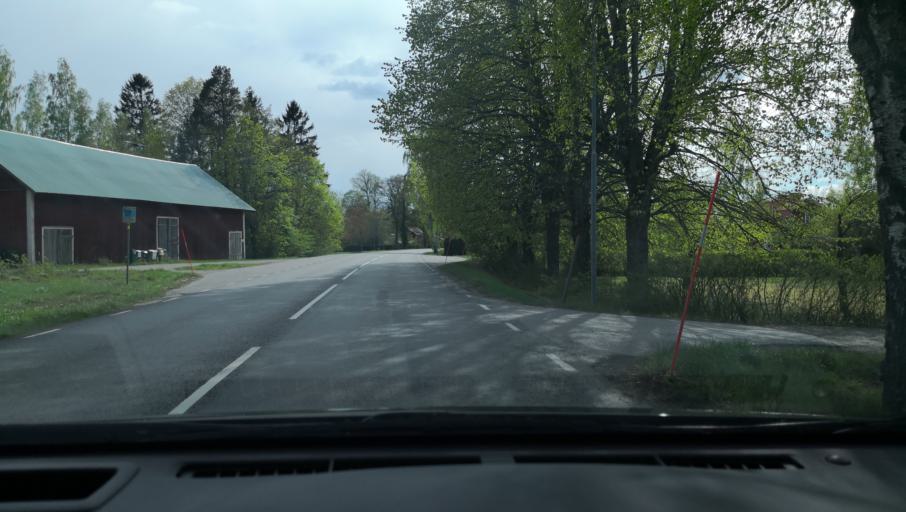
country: SE
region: OErebro
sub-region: Kumla Kommun
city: Kumla
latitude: 59.0816
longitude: 15.1555
